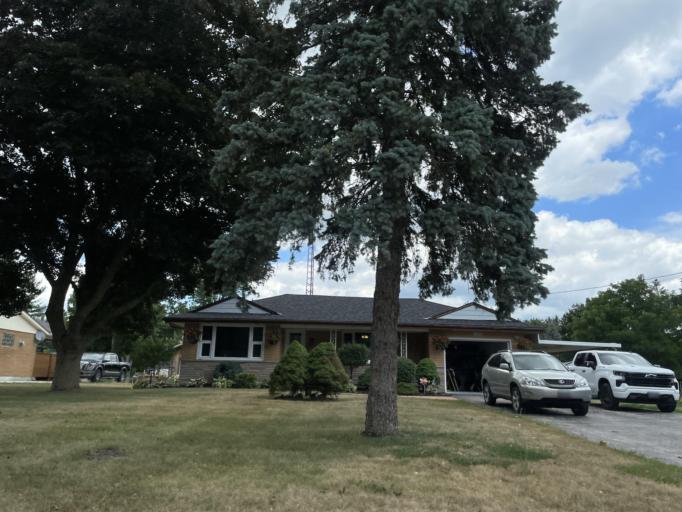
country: CA
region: Ontario
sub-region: Wellington County
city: Guelph
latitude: 43.5331
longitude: -80.3893
